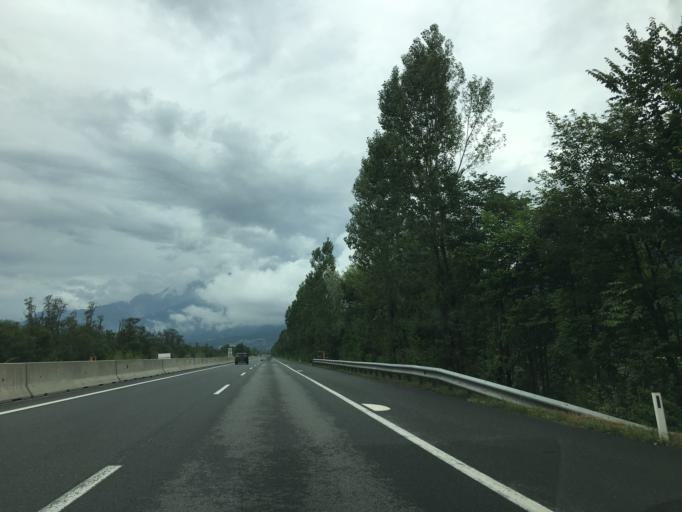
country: AT
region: Tyrol
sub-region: Politischer Bezirk Innsbruck Land
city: Polling in Tirol
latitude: 47.2905
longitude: 11.1496
